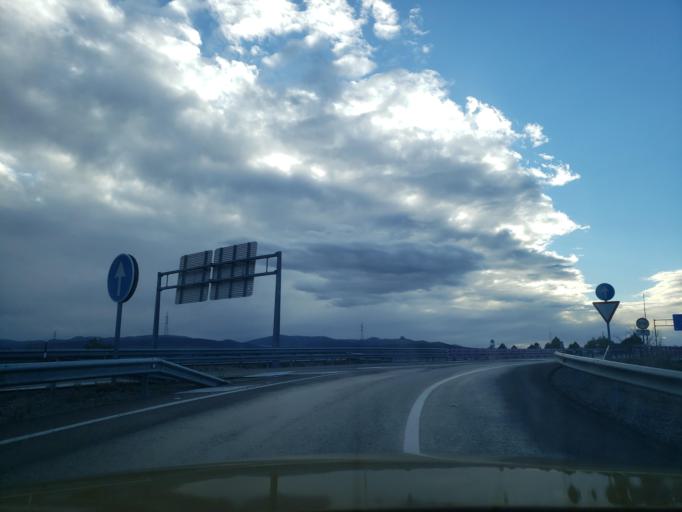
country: ES
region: Castille-La Mancha
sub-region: Province of Toledo
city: Madridejos
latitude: 39.4473
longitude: -3.5250
